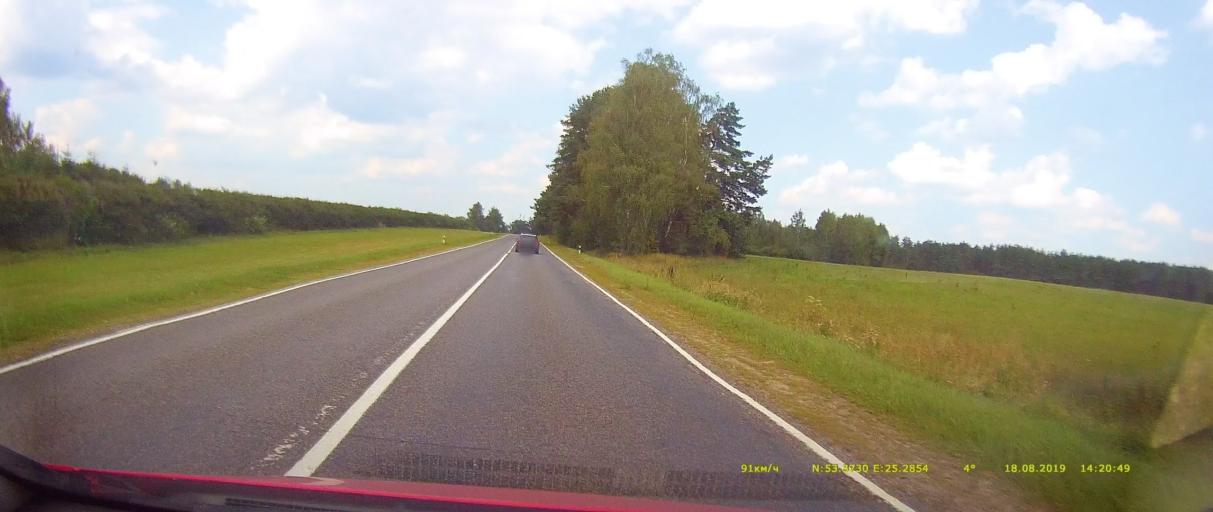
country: BY
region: Grodnenskaya
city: Dzyatlava
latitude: 53.3882
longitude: 25.3014
